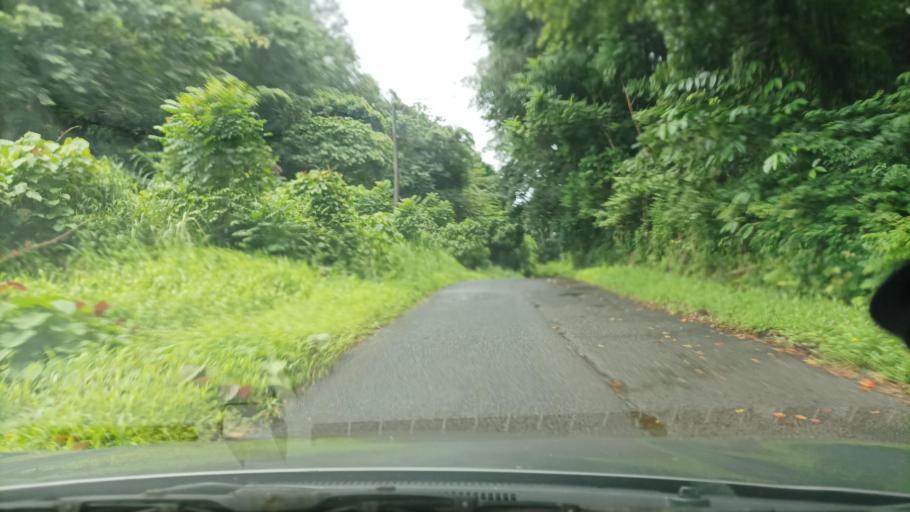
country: FM
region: Pohnpei
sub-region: Madolenihm Municipality
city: Madolenihm Municipality Government
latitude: 6.8399
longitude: 158.2993
